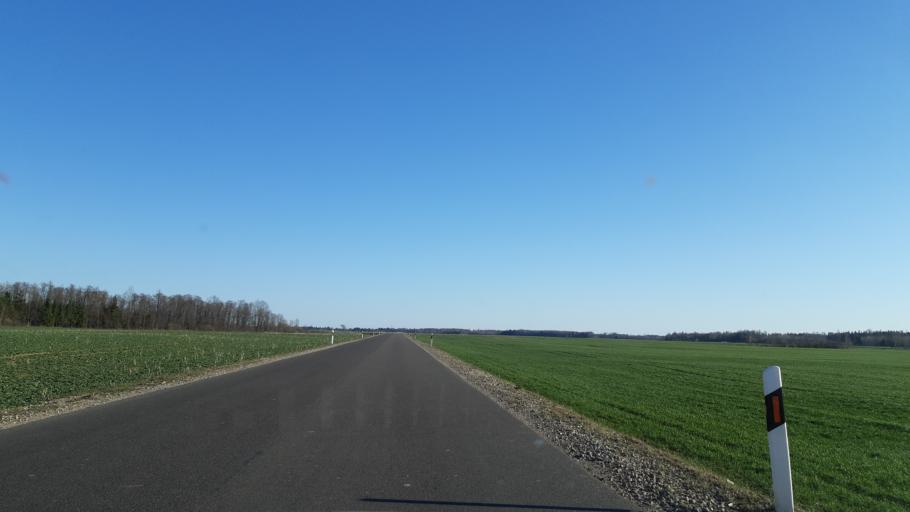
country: LT
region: Kauno apskritis
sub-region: Kaunas
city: Sargenai
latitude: 55.0255
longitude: 23.7611
